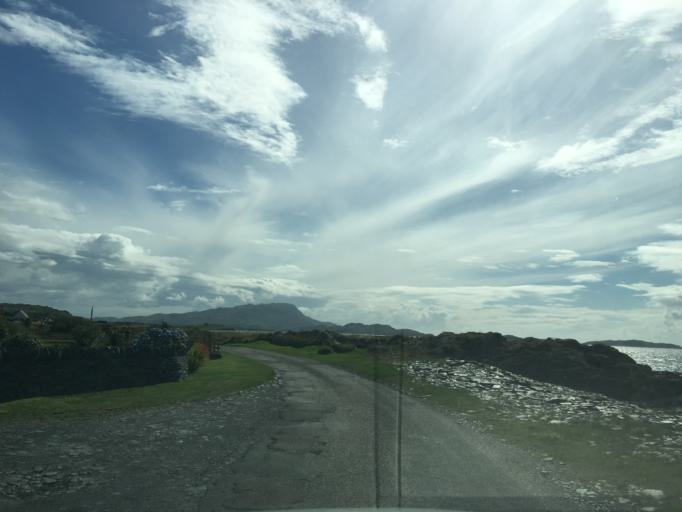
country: GB
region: Scotland
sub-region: Argyll and Bute
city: Isle Of Mull
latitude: 56.2539
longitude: -5.6538
